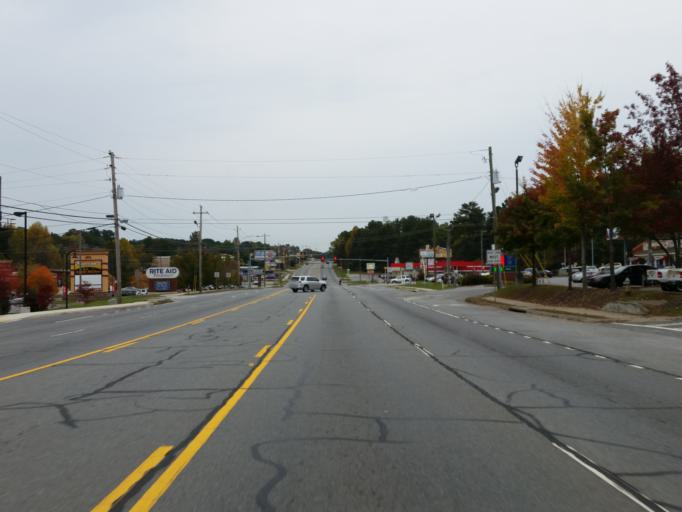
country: US
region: Georgia
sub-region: Cherokee County
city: Woodstock
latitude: 34.0676
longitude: -84.5213
